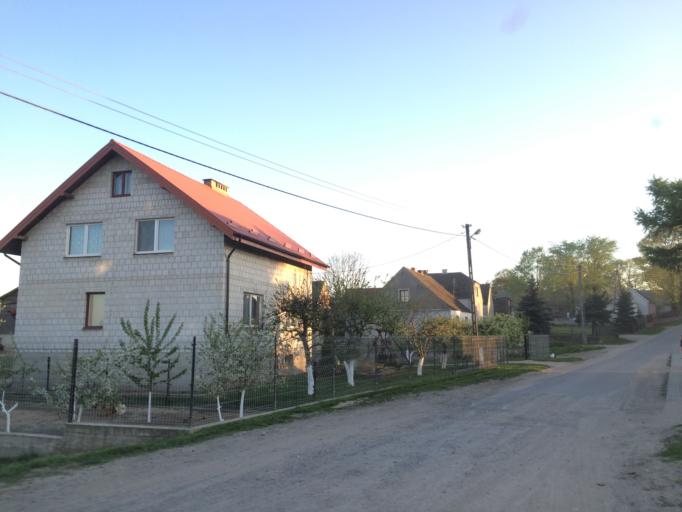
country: PL
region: Warmian-Masurian Voivodeship
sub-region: Powiat dzialdowski
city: Rybno
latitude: 53.4766
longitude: 19.8729
